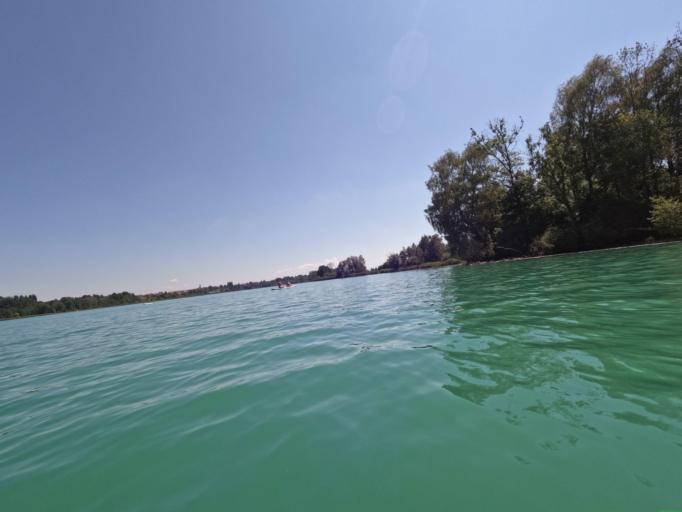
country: DE
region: Bavaria
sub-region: Upper Bavaria
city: Taching am See
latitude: 47.9600
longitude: 12.7349
